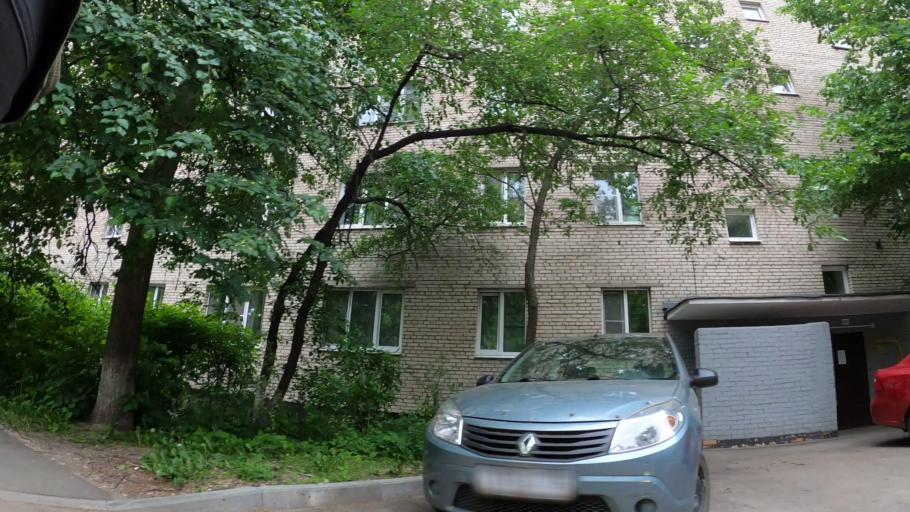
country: RU
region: Moskovskaya
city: Yubileyny
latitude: 55.9443
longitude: 37.8474
